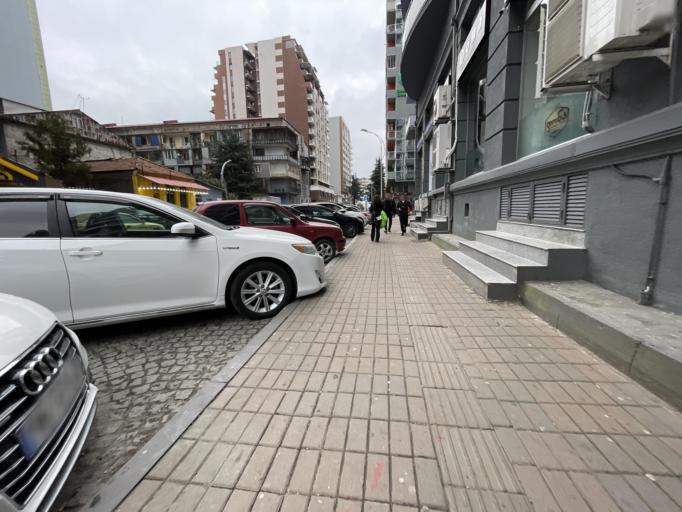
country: GE
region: Ajaria
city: Batumi
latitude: 41.6451
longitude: 41.6291
